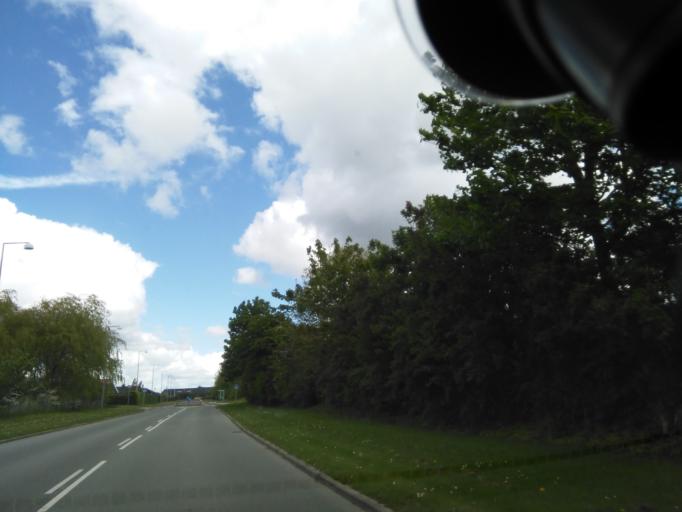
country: DK
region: Central Jutland
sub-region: Skanderborg Kommune
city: Horning
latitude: 56.0838
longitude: 10.0223
